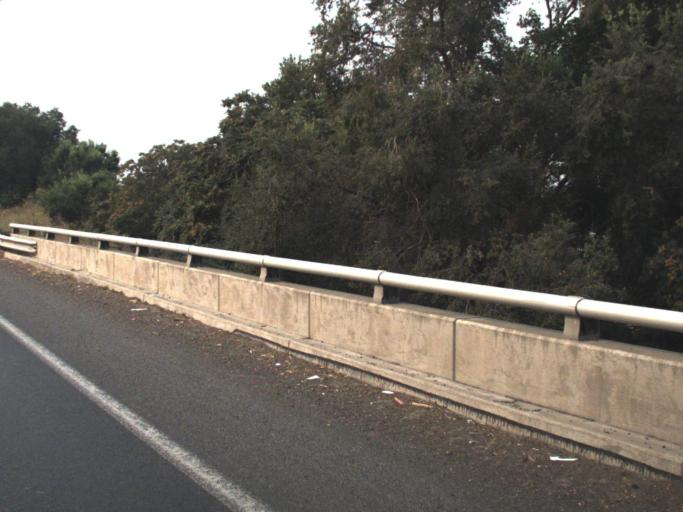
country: US
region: Washington
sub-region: Yakima County
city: Granger
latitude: 46.3426
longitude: -120.1846
